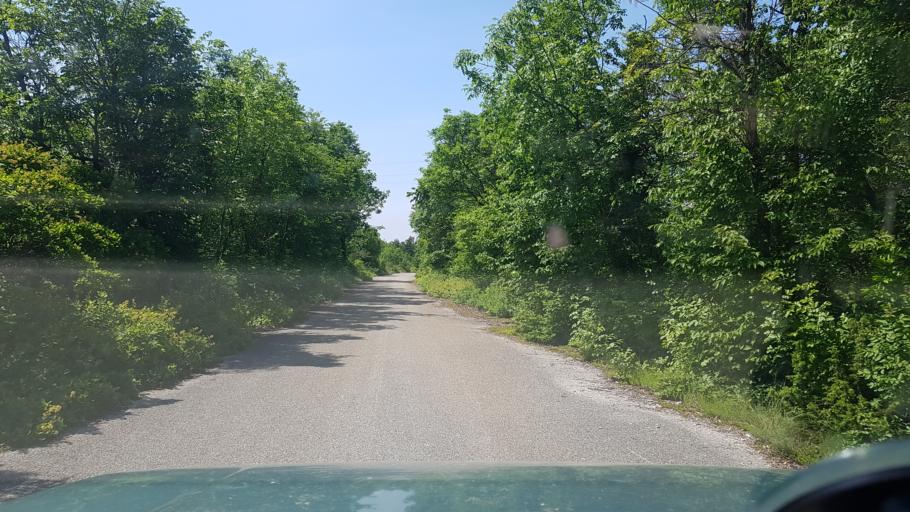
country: IT
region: Friuli Venezia Giulia
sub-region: Provincia di Trieste
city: Villa Opicina
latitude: 45.7095
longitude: 13.7784
